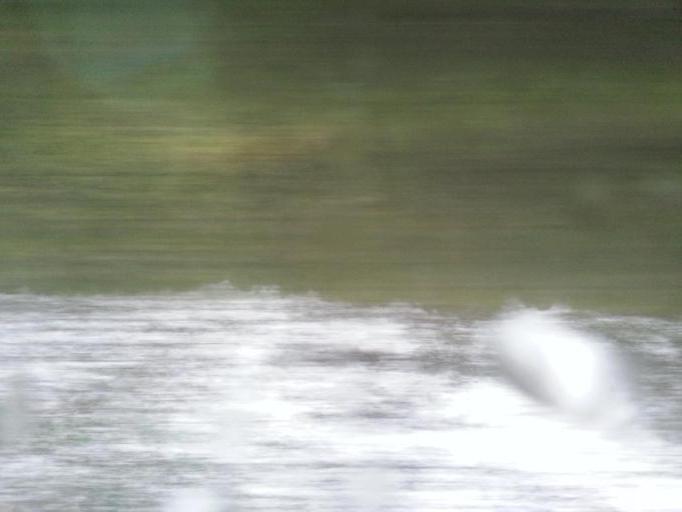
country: NO
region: Sor-Trondelag
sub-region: Oppdal
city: Oppdal
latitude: 62.6127
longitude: 9.7504
